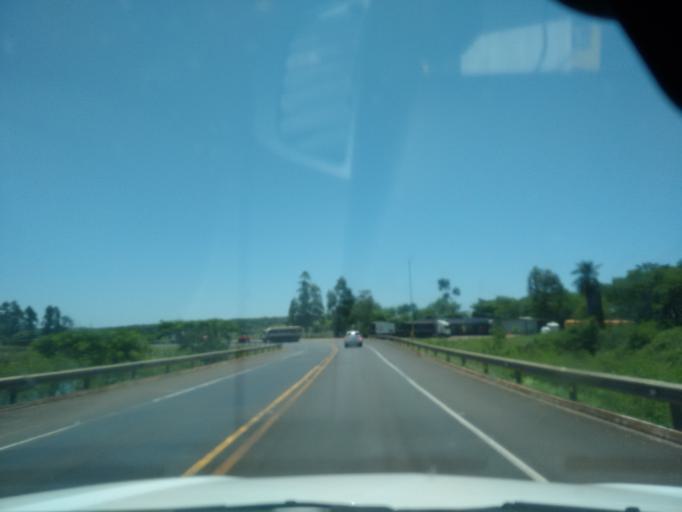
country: PY
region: Canindeyu
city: Salto del Guaira
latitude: -24.0442
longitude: -54.2724
